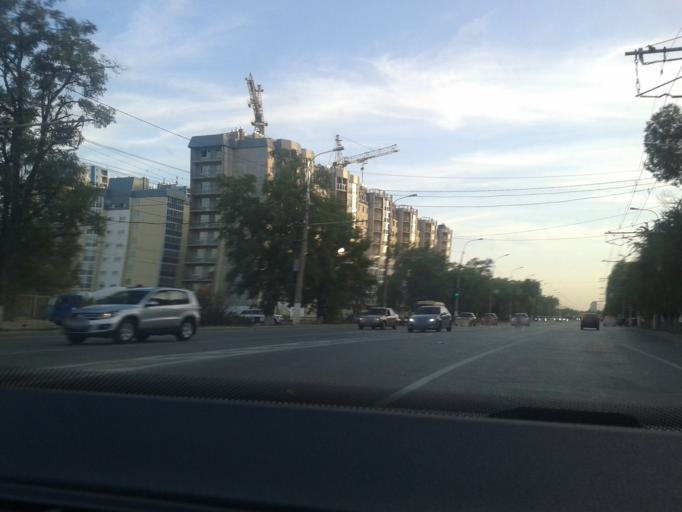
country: RU
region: Volgograd
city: Krasnoslobodsk
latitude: 48.7347
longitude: 44.5431
